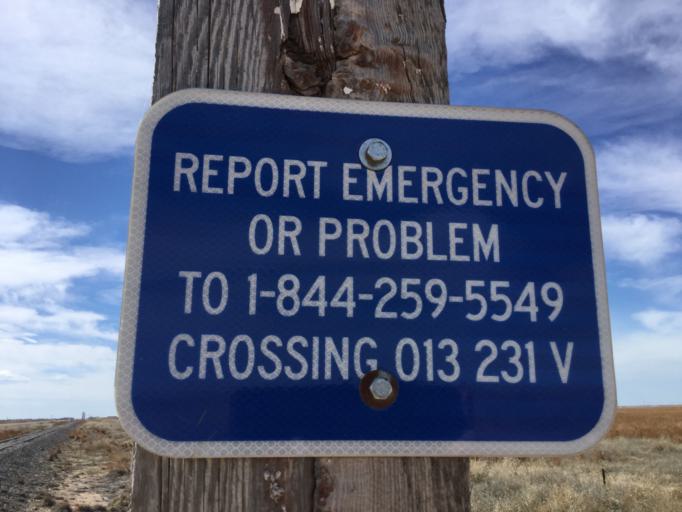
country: US
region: Kansas
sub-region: Stevens County
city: Hugoton
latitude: 37.1344
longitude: -101.5739
